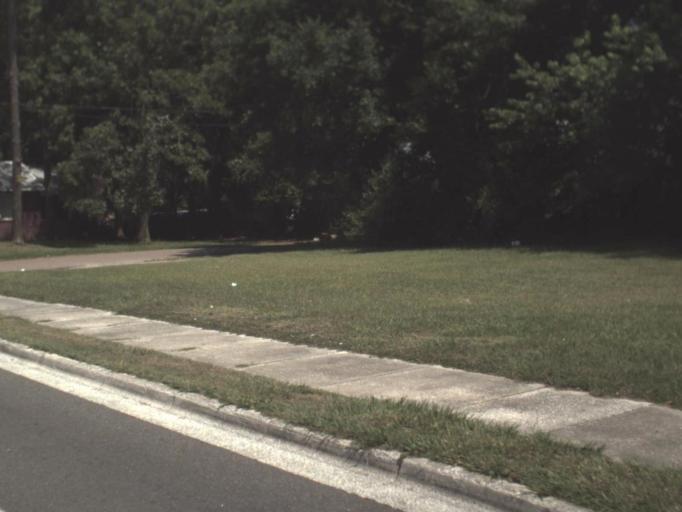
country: US
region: Florida
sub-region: Duval County
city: Jacksonville
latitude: 30.4145
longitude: -81.6938
